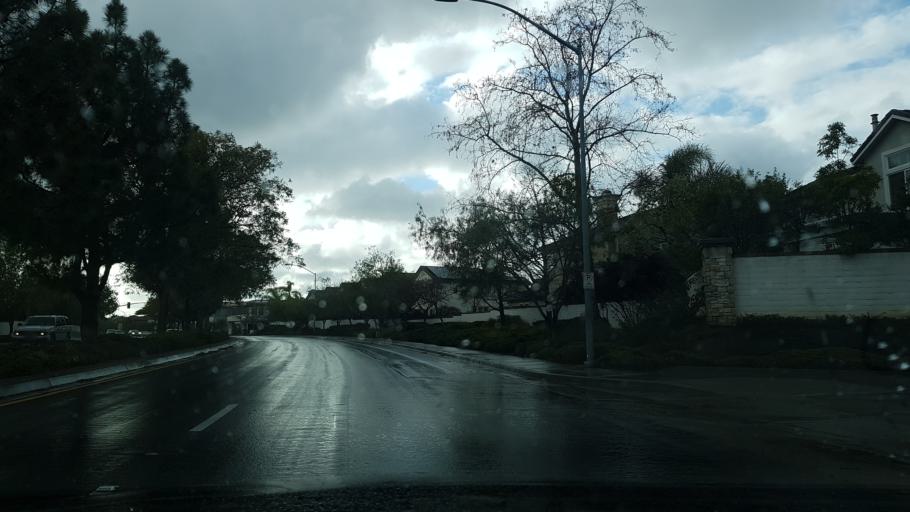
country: US
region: California
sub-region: San Diego County
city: Fairbanks Ranch
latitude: 32.9294
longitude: -117.1951
